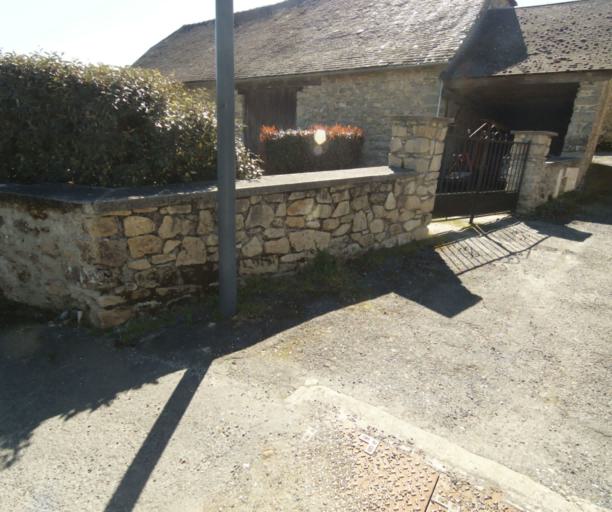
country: FR
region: Limousin
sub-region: Departement de la Correze
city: Saint-Mexant
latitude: 45.3098
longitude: 1.6364
